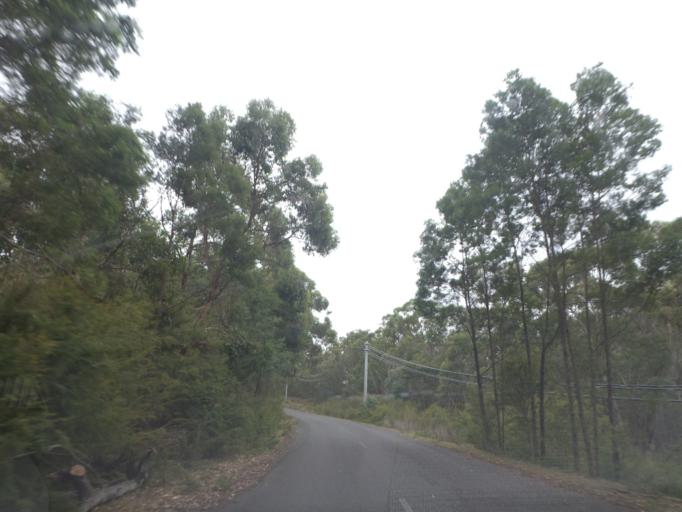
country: AU
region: Victoria
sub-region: Yarra Ranges
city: Chirnside Park
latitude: -37.6850
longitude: 145.3118
